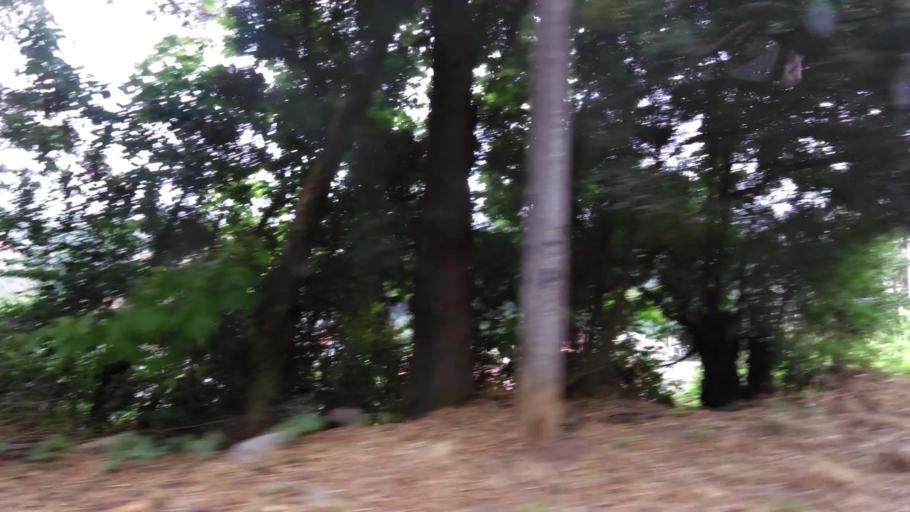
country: CL
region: Biobio
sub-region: Provincia de Concepcion
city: Concepcion
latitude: -36.8343
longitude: -73.0375
